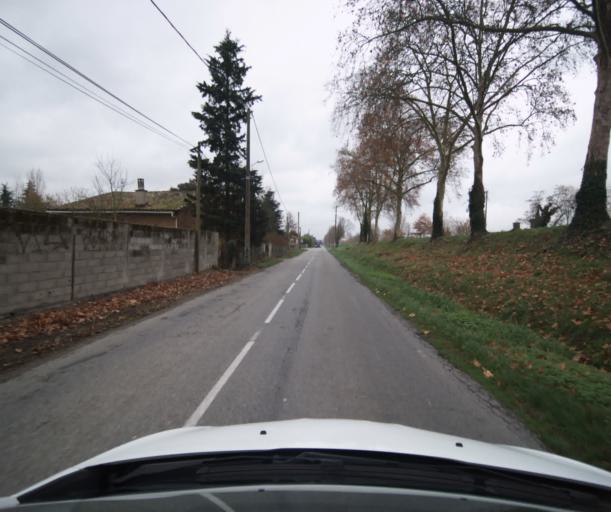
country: FR
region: Midi-Pyrenees
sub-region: Departement du Tarn-et-Garonne
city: Castelsarrasin
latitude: 44.0346
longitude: 1.1268
